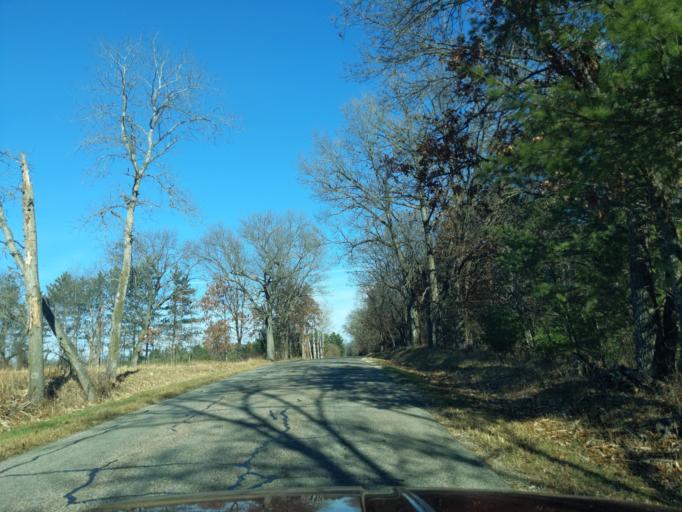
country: US
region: Wisconsin
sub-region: Waushara County
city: Silver Lake
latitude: 44.0719
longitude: -89.1938
